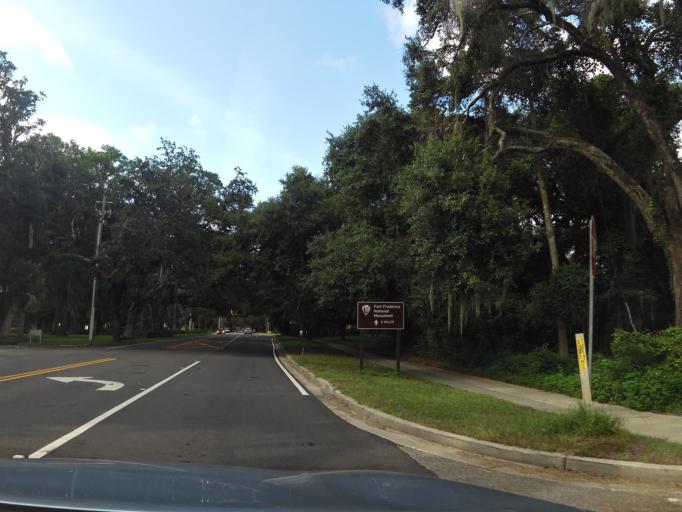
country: US
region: Georgia
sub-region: Glynn County
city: Saint Simon Mills
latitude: 31.1823
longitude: -81.3773
